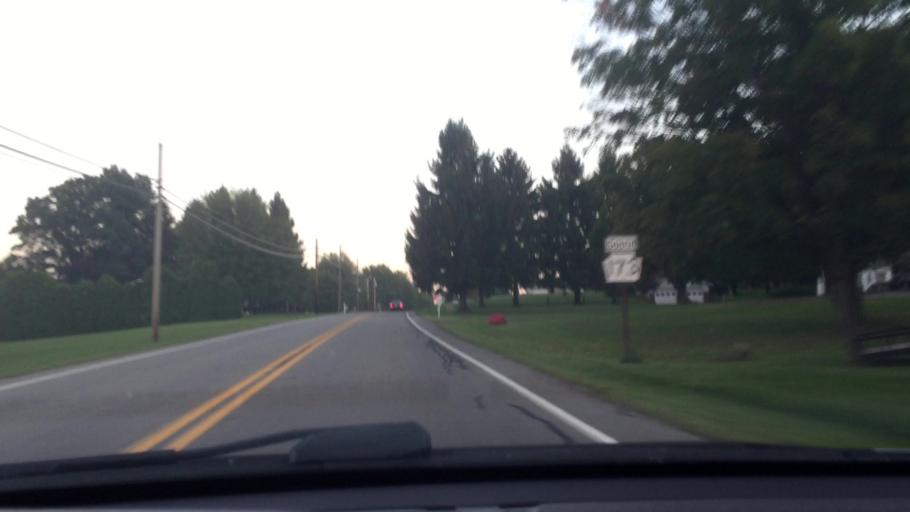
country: US
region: Pennsylvania
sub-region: Mercer County
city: Grove City
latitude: 41.1191
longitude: -80.0606
